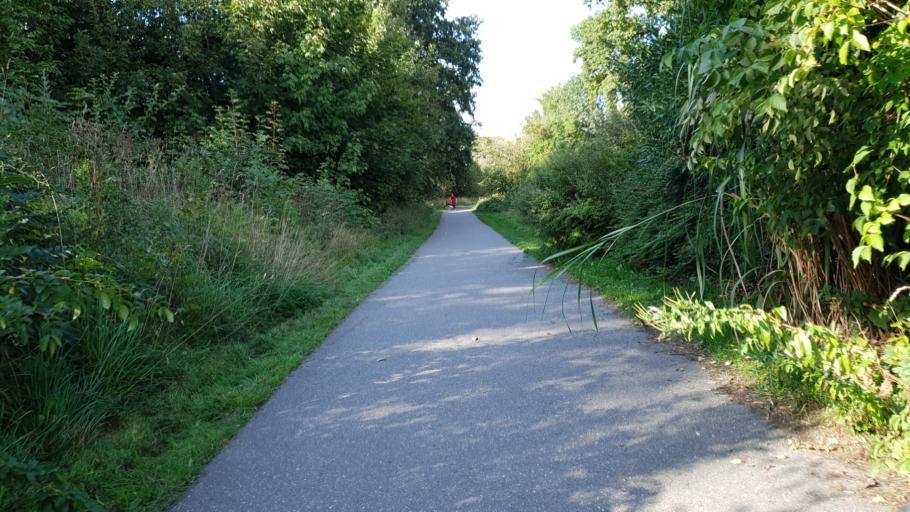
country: DE
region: Schleswig-Holstein
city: Ottendorf
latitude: 54.3561
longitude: 10.0664
